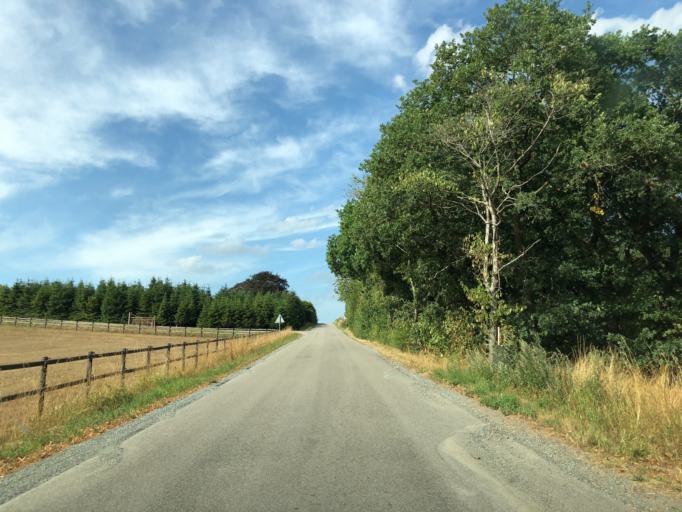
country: DK
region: South Denmark
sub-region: Vejle Kommune
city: Egtved
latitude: 55.6718
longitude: 9.3031
